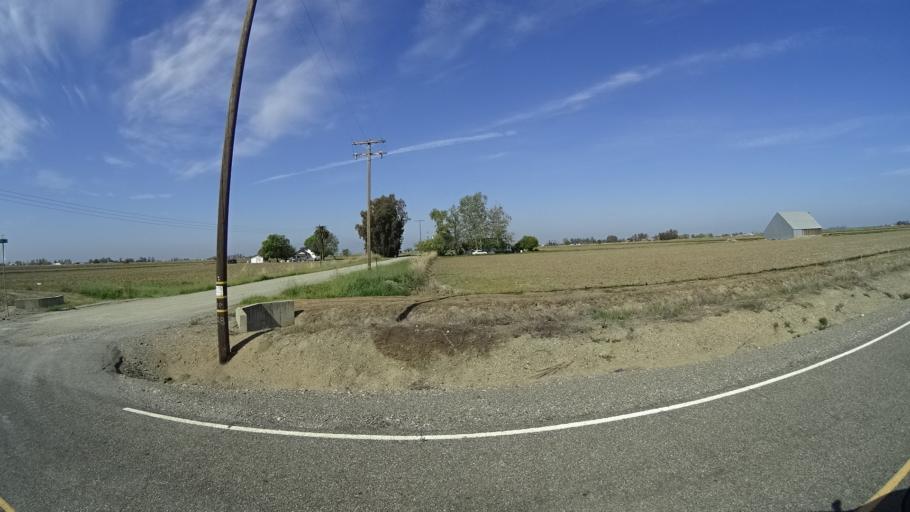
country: US
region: California
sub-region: Glenn County
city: Hamilton City
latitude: 39.5945
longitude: -122.0367
